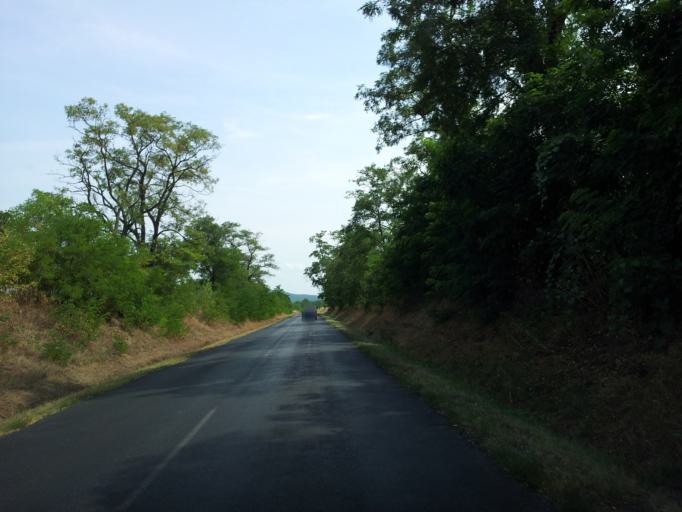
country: HU
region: Veszprem
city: Tapolca
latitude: 46.8580
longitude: 17.4569
